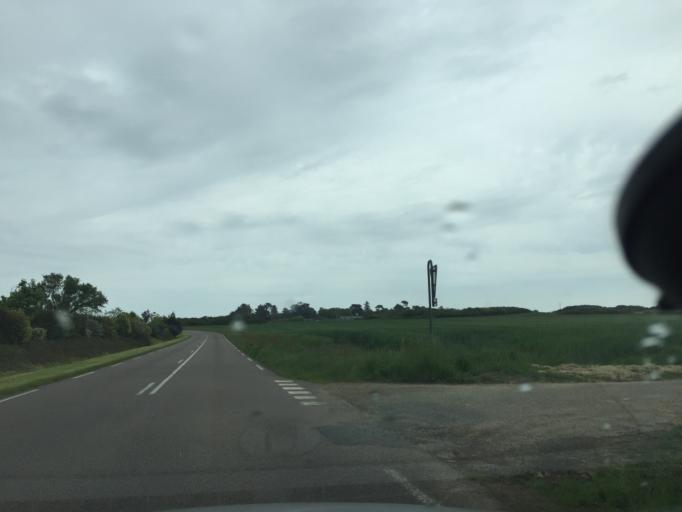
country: FR
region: Brittany
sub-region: Departement des Cotes-d'Armor
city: Plurien
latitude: 48.6562
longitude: -2.3501
